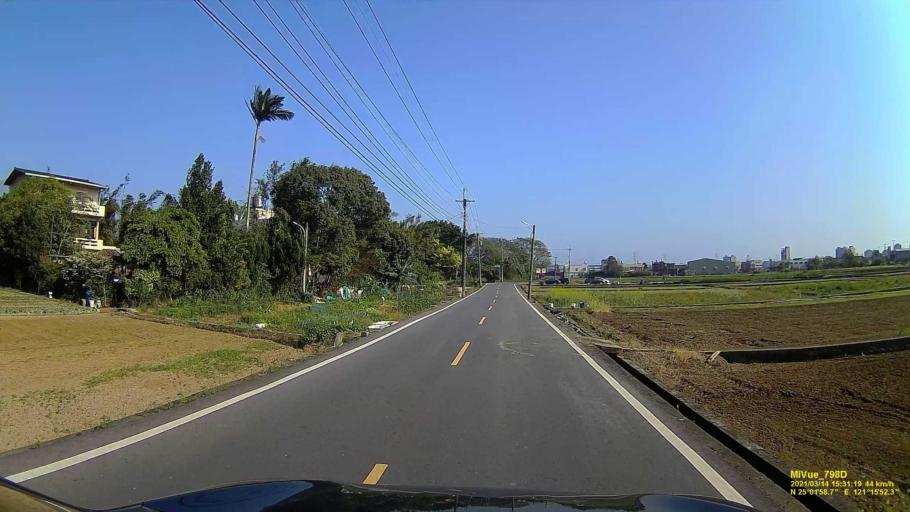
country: TW
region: Taiwan
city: Taoyuan City
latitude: 25.0327
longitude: 121.2648
